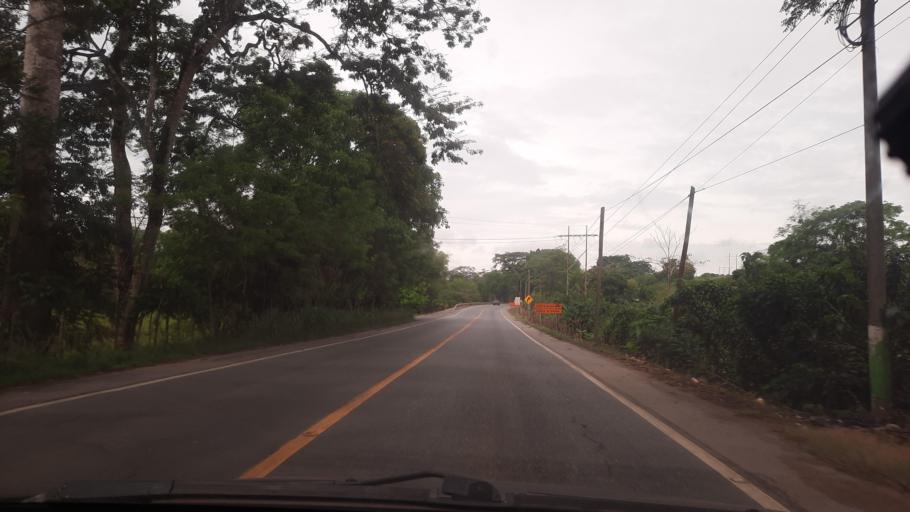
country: GT
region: Izabal
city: Morales
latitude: 15.5088
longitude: -88.8074
